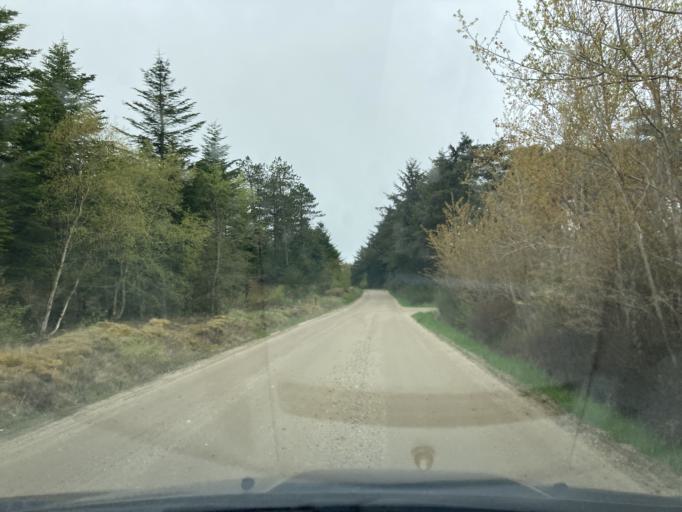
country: DK
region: Central Jutland
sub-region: Lemvig Kommune
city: Thyboron
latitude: 56.8209
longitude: 8.2671
